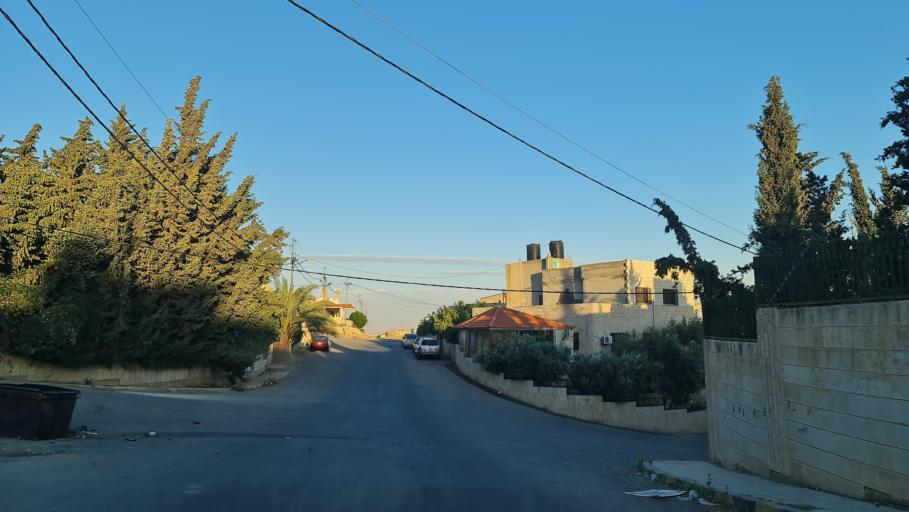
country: JO
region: Zarqa
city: Zarqa
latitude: 32.0898
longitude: 36.0182
